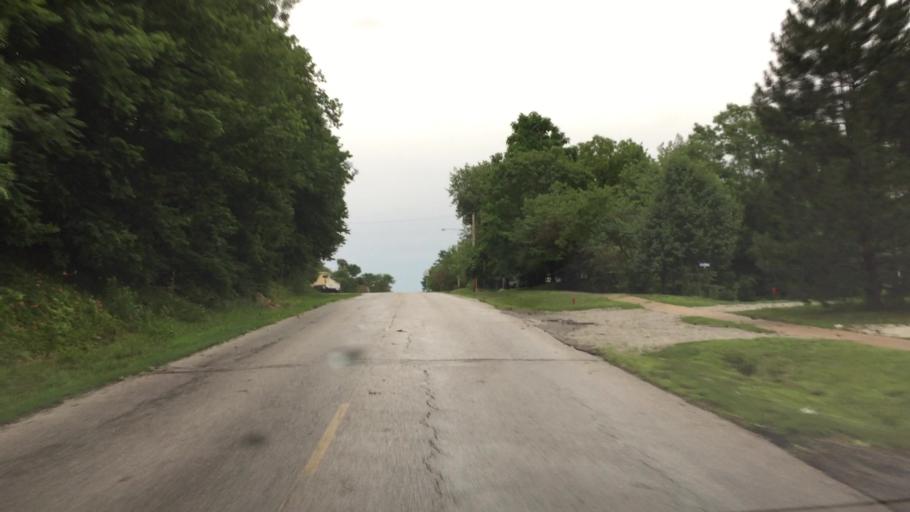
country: US
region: Illinois
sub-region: Hancock County
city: Hamilton
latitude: 40.3932
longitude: -91.3529
